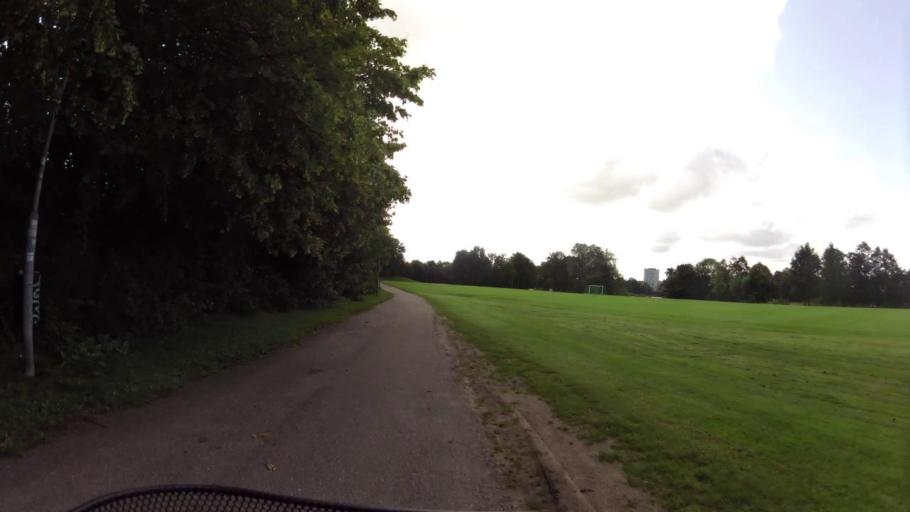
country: SE
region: OEstergoetland
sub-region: Linkopings Kommun
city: Linkoping
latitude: 58.4173
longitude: 15.6304
